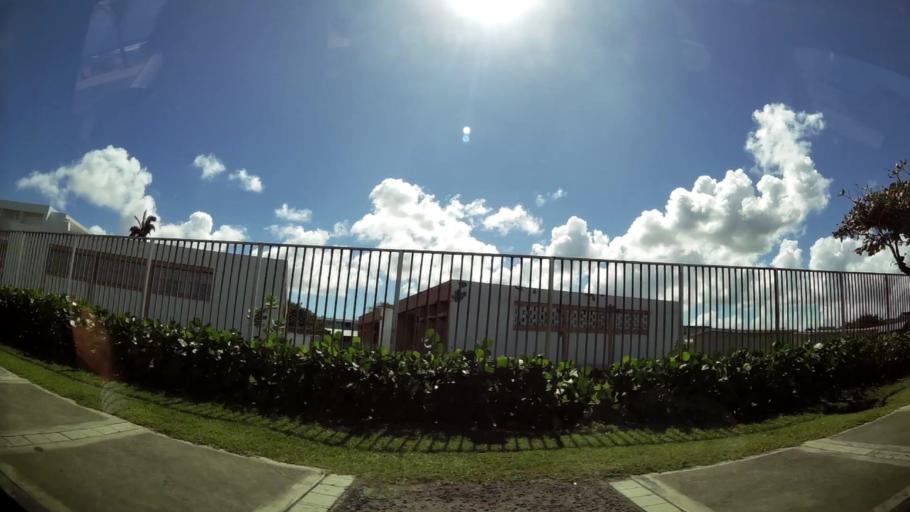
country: GP
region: Guadeloupe
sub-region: Guadeloupe
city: Le Moule
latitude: 16.3332
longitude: -61.3527
